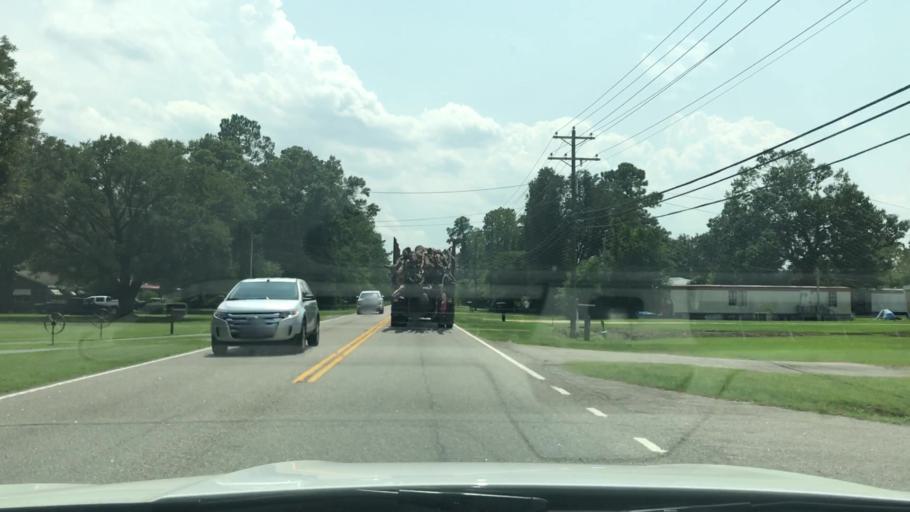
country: US
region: South Carolina
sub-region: Georgetown County
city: Georgetown
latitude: 33.4319
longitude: -79.2781
